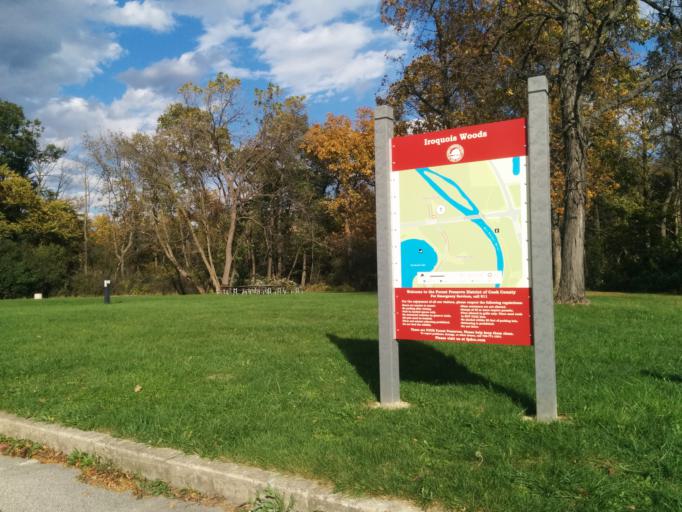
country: US
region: Illinois
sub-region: Cook County
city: Park Ridge
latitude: 42.0104
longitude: -87.8638
